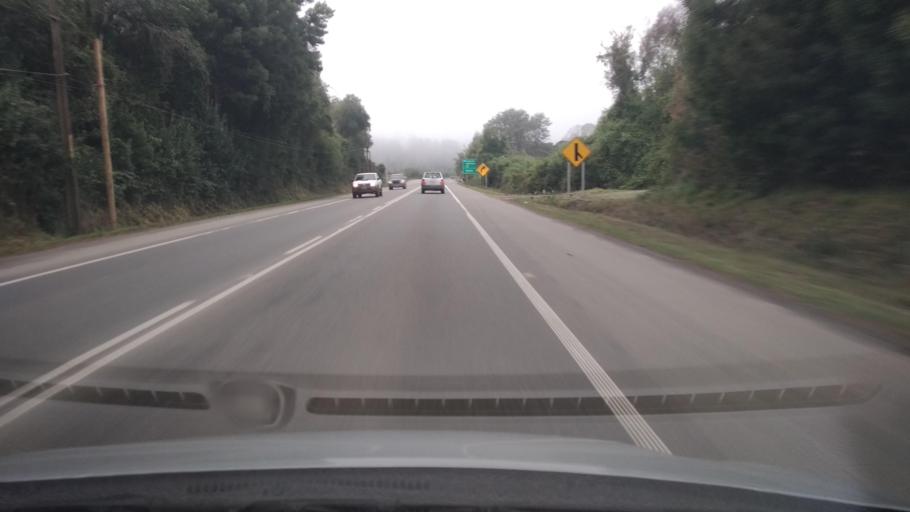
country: CL
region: Los Lagos
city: Las Animas
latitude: -39.7312
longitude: -73.2013
